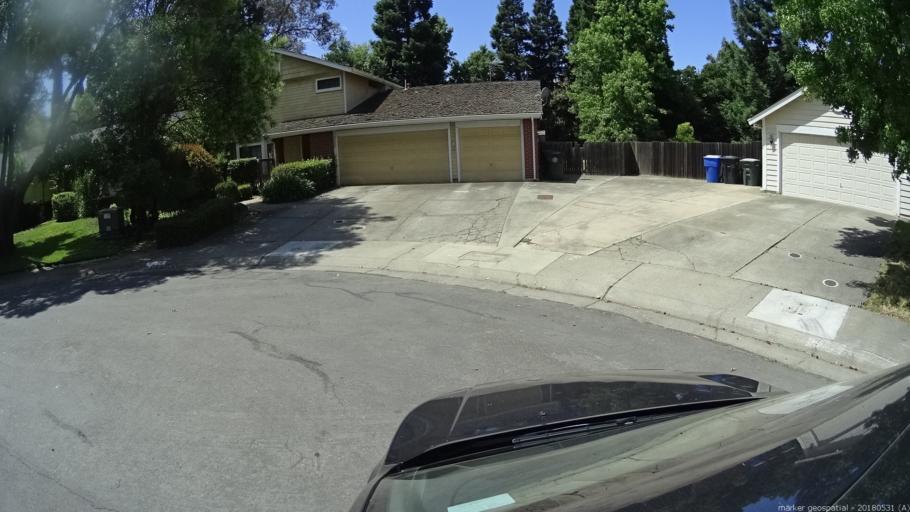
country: US
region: California
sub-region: Yolo County
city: West Sacramento
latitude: 38.6243
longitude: -121.5146
